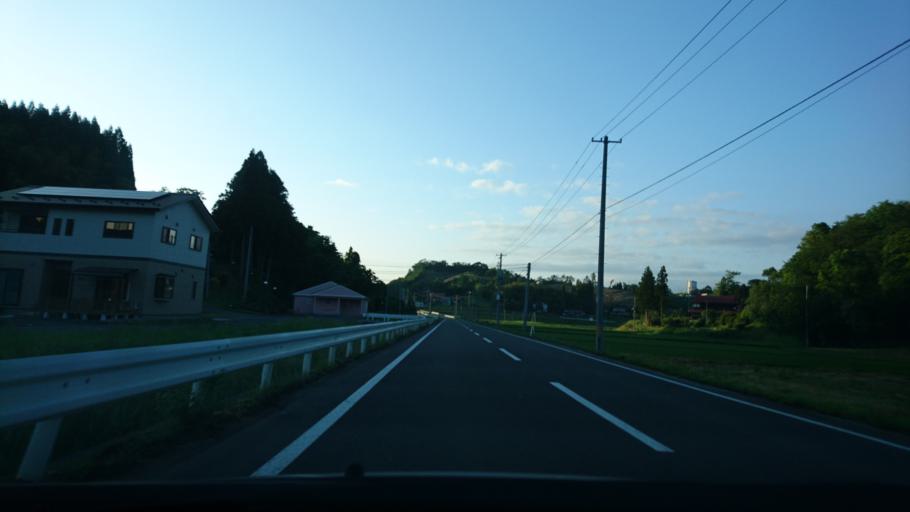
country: JP
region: Iwate
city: Ichinoseki
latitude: 38.8963
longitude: 141.1594
